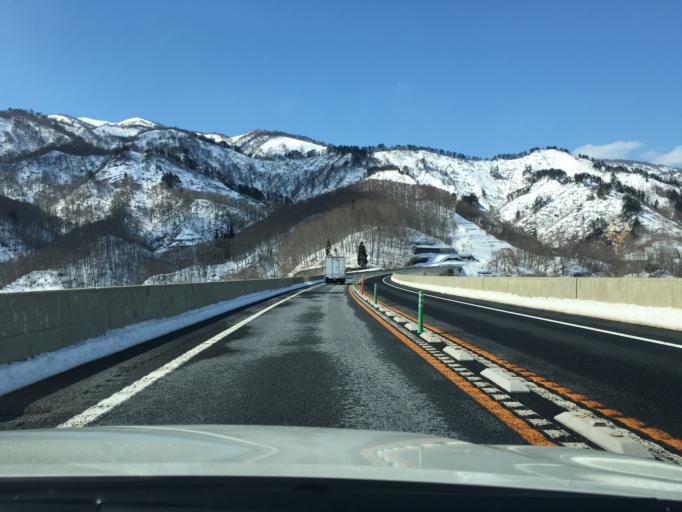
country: JP
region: Yamagata
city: Sagae
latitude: 38.4473
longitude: 139.9971
